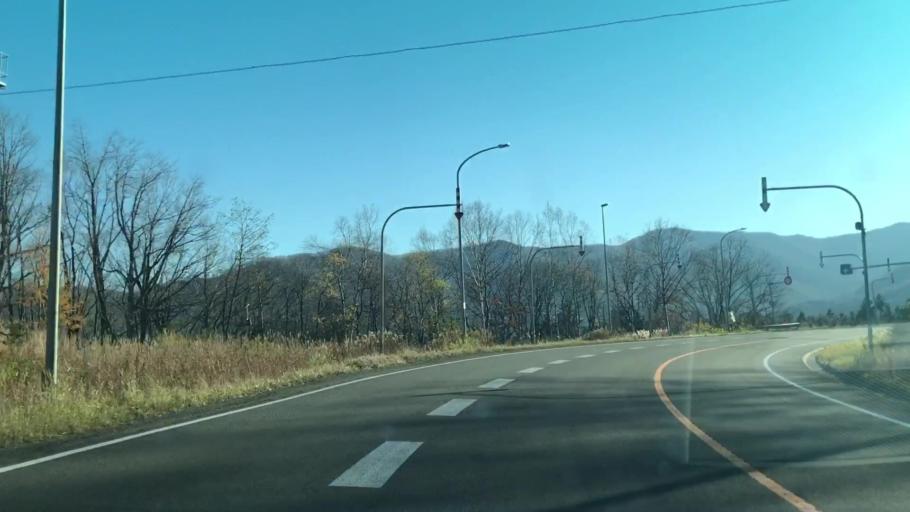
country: JP
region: Hokkaido
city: Otofuke
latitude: 42.9697
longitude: 142.8050
